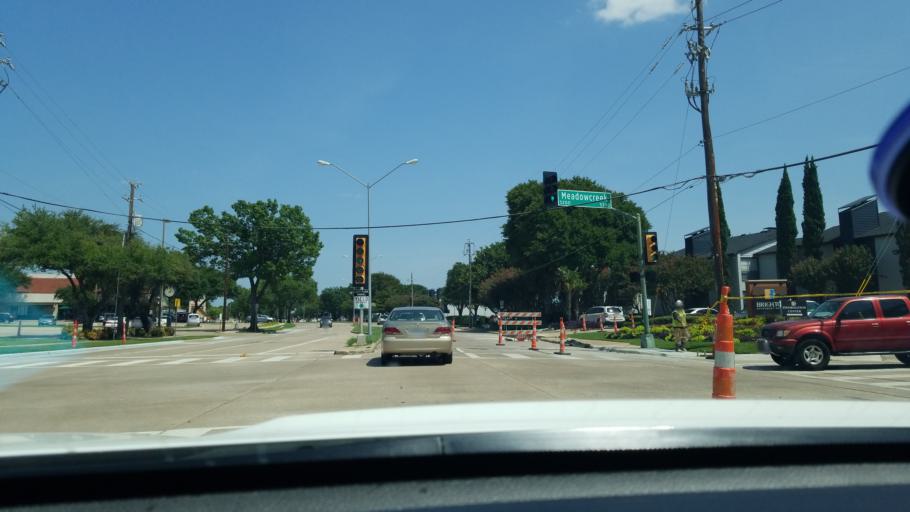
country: US
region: Texas
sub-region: Dallas County
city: Addison
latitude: 32.9625
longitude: -96.7919
